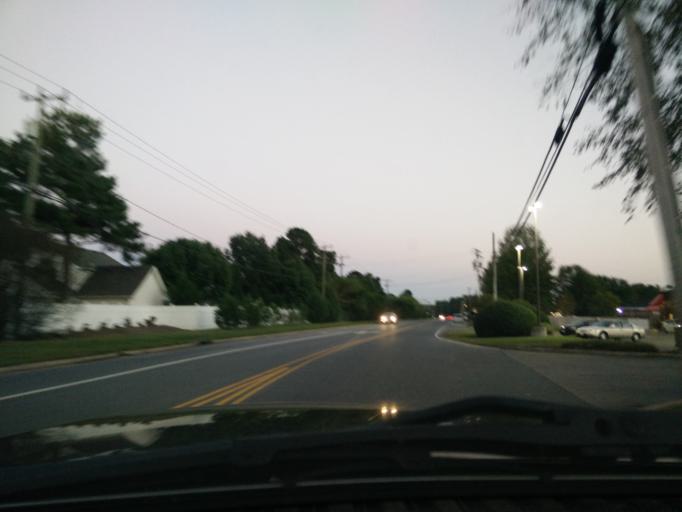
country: US
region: Virginia
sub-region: City of Chesapeake
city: Chesapeake
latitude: 36.7552
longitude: -76.2476
